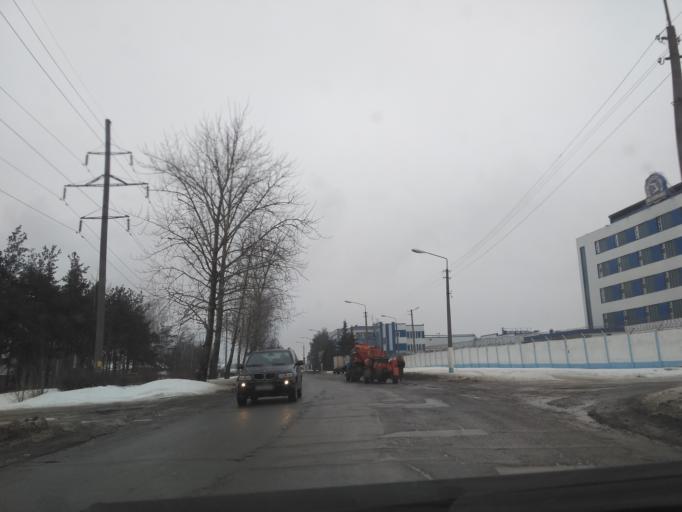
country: BY
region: Minsk
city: Horad Barysaw
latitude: 54.1982
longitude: 28.5121
